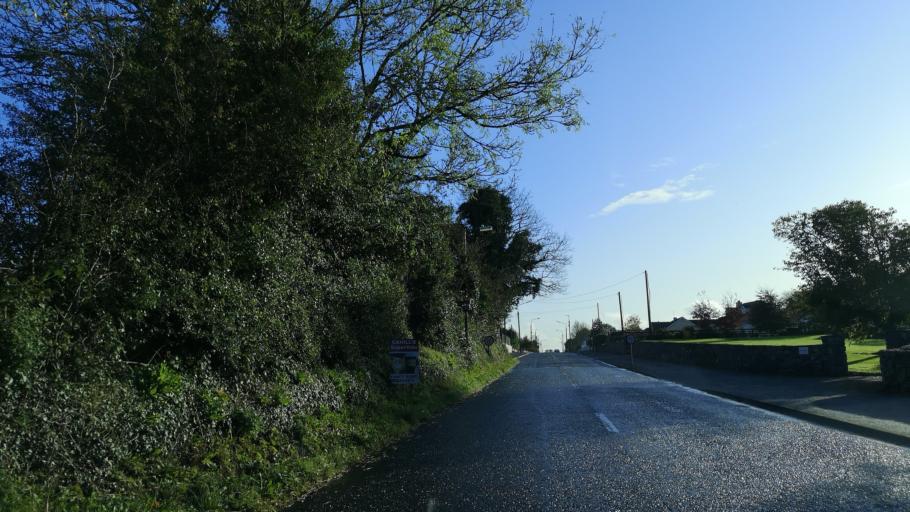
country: IE
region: Connaught
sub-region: Roscommon
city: Castlerea
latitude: 53.7773
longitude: -8.4889
